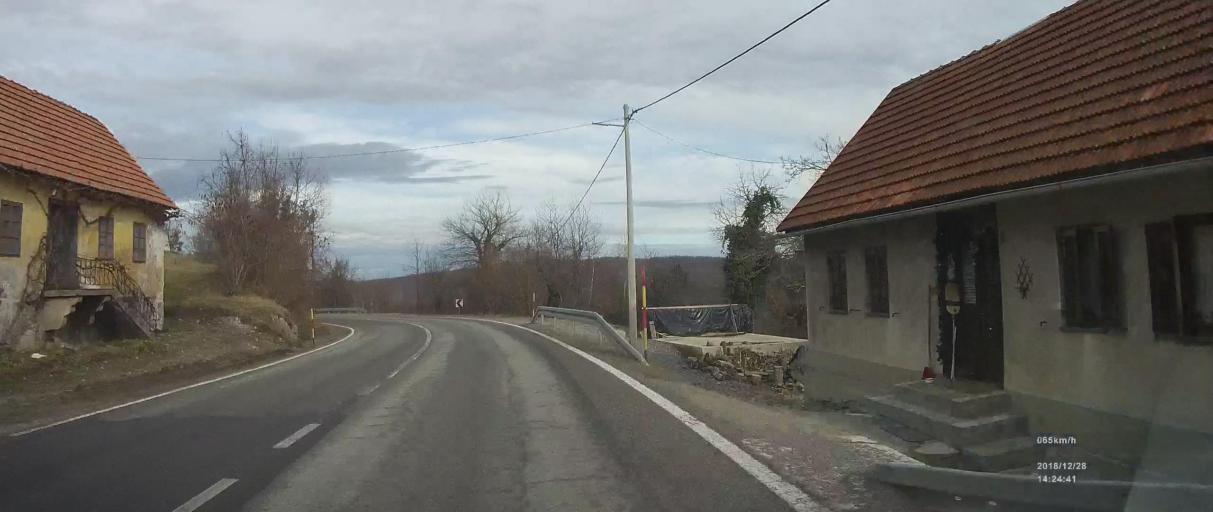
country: HR
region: Primorsko-Goranska
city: Vrbovsko
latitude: 45.3873
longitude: 15.1046
